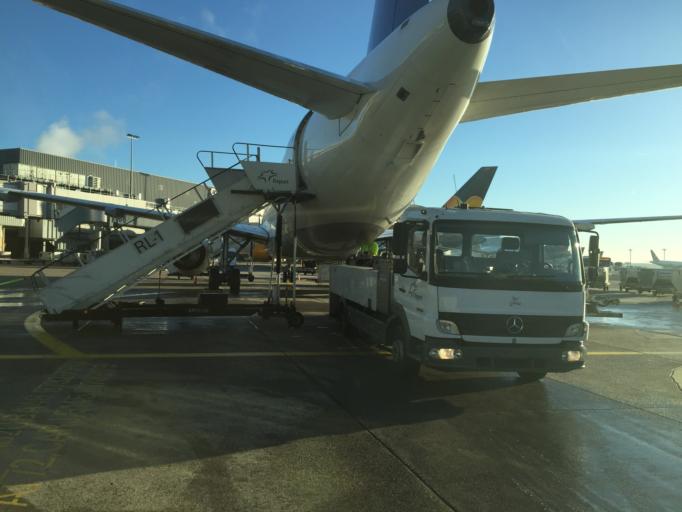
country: DE
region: Hesse
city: Kelsterbach
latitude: 50.0500
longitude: 8.5739
